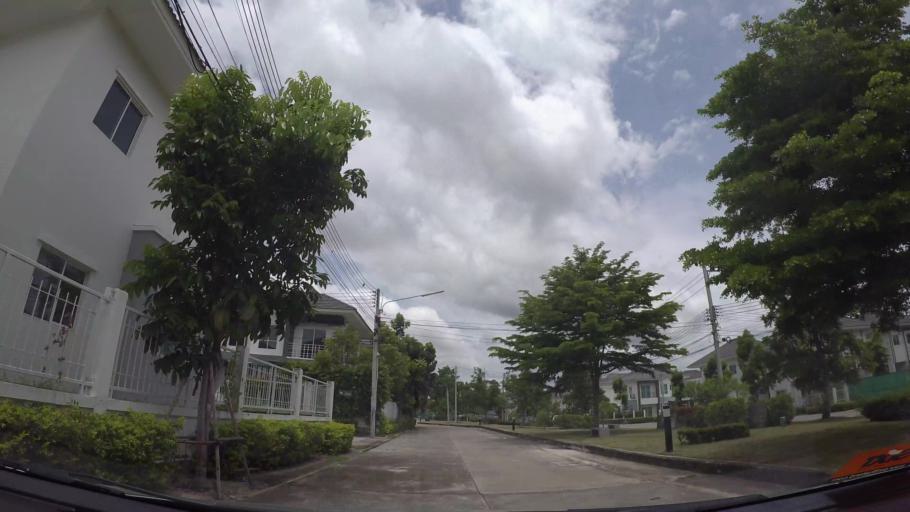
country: TH
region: Chon Buri
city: Si Racha
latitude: 13.1718
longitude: 100.9743
